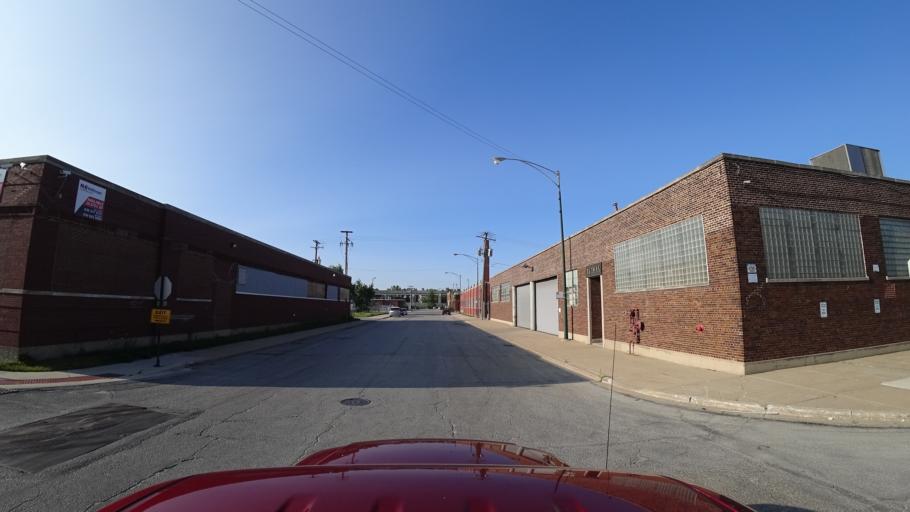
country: US
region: Illinois
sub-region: Cook County
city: Cicero
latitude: 41.8068
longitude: -87.7113
